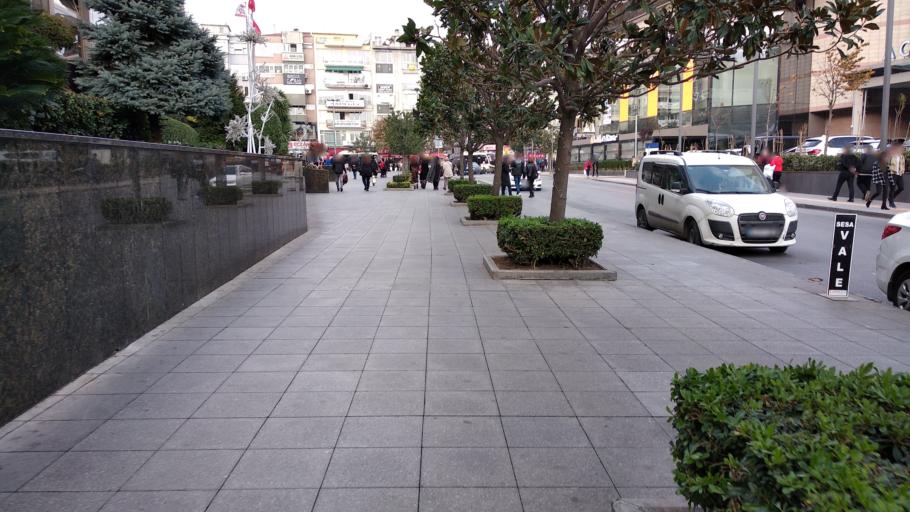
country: TR
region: Istanbul
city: Bahcelievler
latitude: 40.9773
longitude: 28.8724
